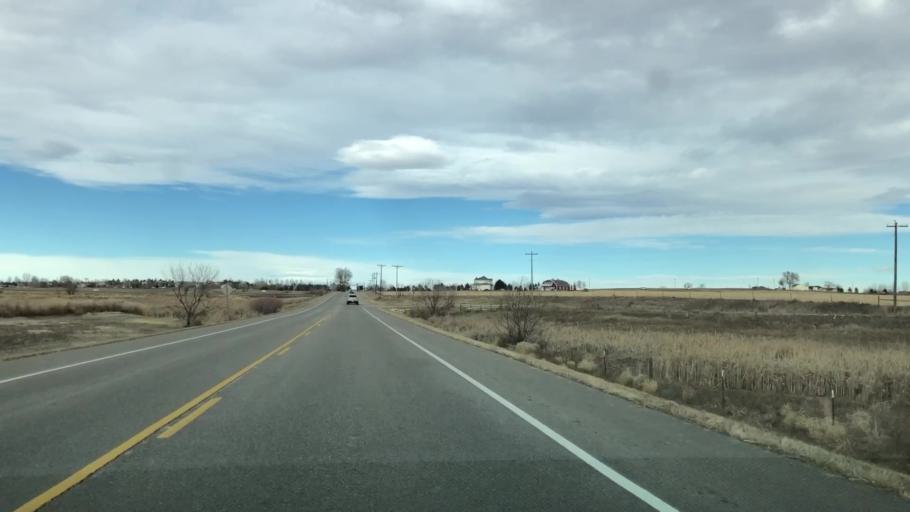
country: US
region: Colorado
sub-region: Weld County
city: Windsor
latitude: 40.5171
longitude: -104.9267
